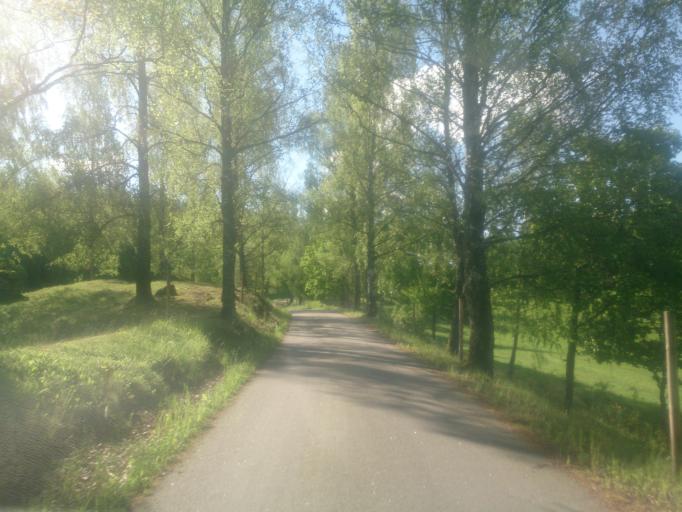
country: SE
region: OEstergoetland
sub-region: Atvidabergs Kommun
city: Atvidaberg
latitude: 58.3037
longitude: 16.0763
